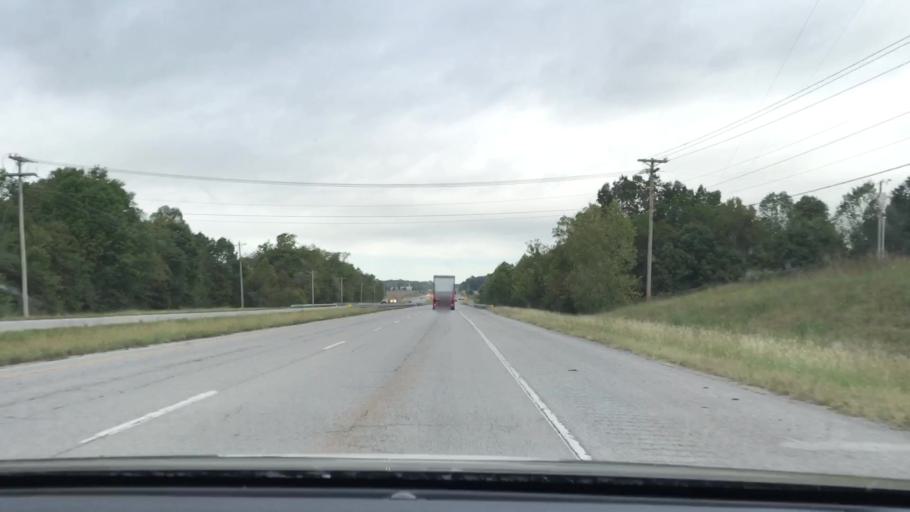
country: US
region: Kentucky
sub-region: Christian County
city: Hopkinsville
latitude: 36.8317
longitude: -87.5227
